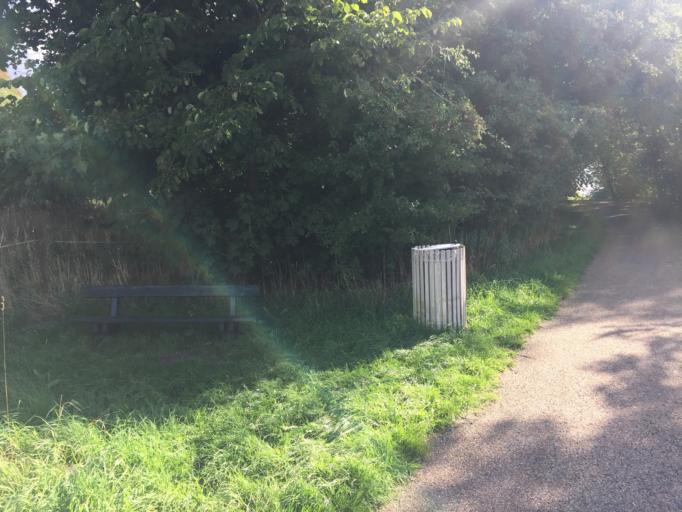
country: DK
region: Capital Region
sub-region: Herlev Kommune
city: Herlev
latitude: 55.7516
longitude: 12.4360
